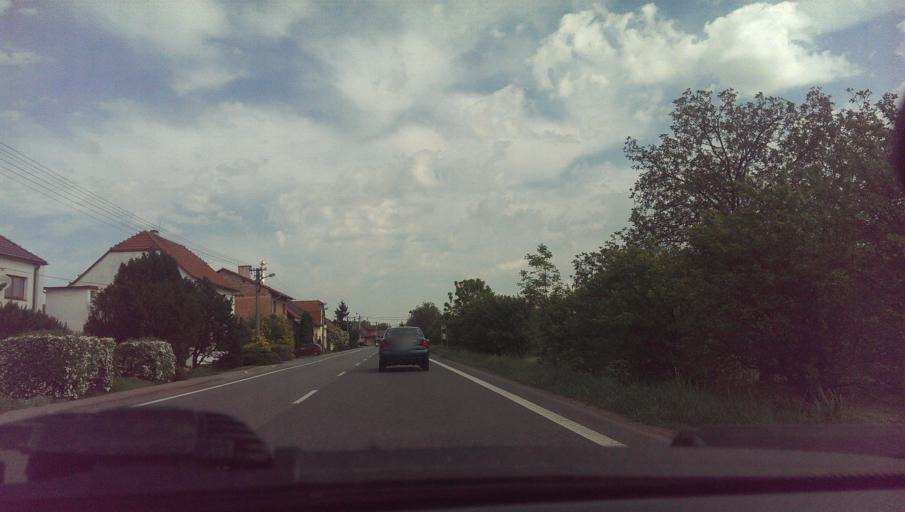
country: CZ
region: Zlin
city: Babice
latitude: 49.1164
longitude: 17.4702
